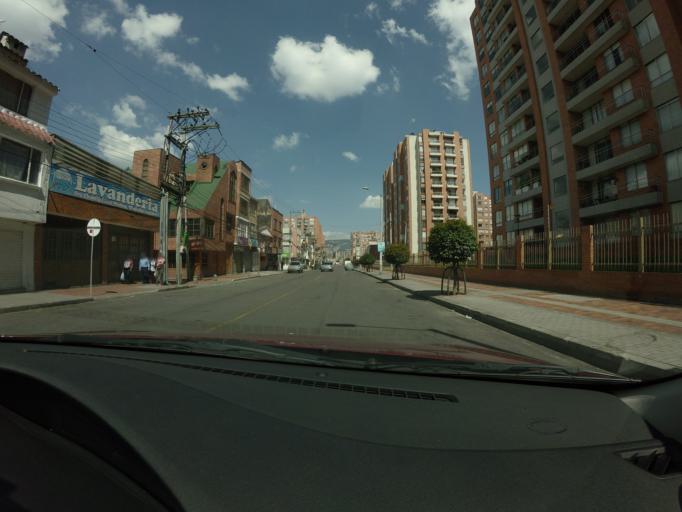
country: CO
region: Cundinamarca
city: Cota
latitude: 4.7439
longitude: -74.0641
